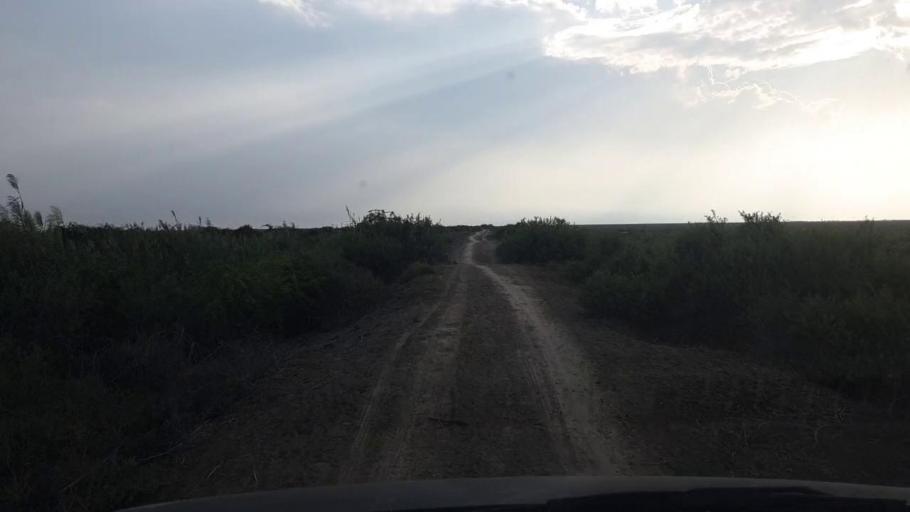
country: PK
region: Sindh
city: Badin
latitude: 24.4430
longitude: 68.6774
